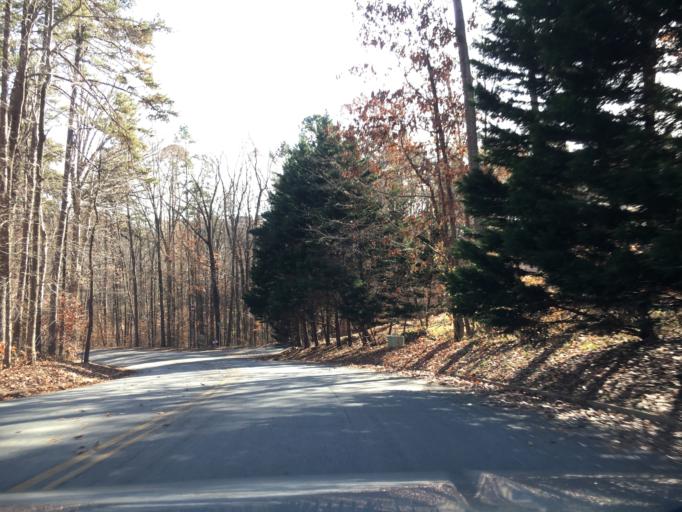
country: US
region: Virginia
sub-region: Halifax County
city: South Boston
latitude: 36.7106
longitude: -78.9143
